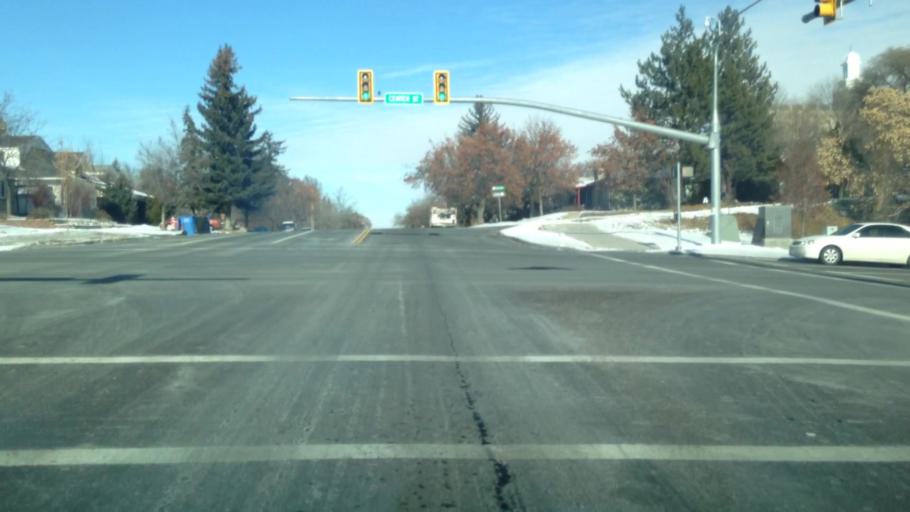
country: US
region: Utah
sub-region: Cache County
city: Logan
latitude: 41.7311
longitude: -111.8298
